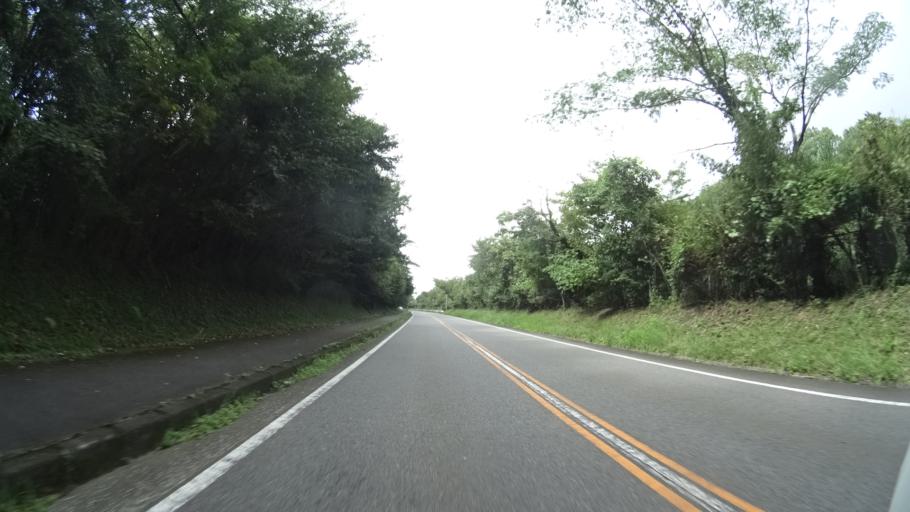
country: JP
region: Oita
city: Beppu
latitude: 33.3483
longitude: 131.4325
